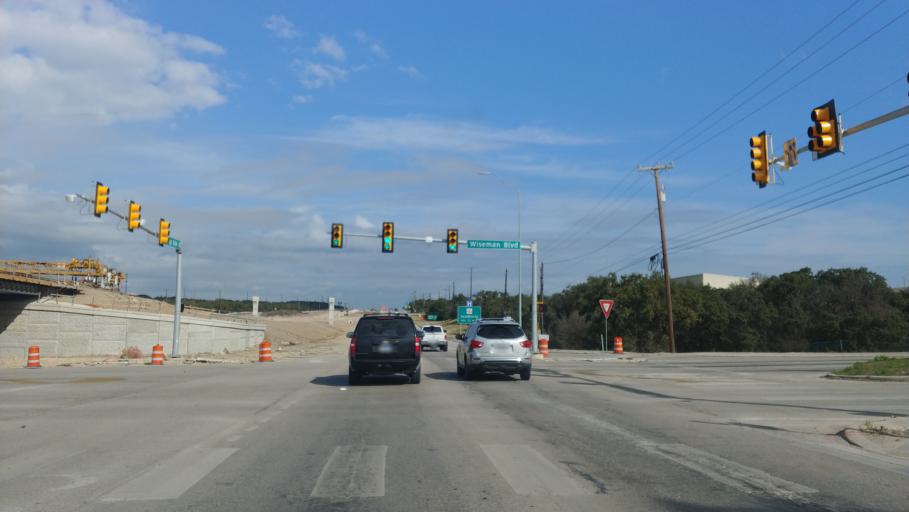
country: US
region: Texas
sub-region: Bexar County
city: Leon Valley
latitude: 29.4652
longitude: -98.7109
